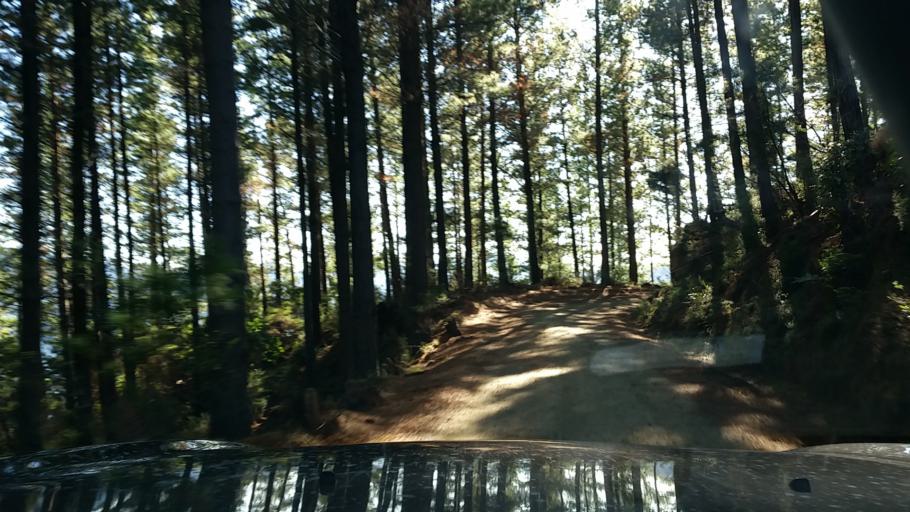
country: NZ
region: Marlborough
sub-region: Marlborough District
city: Picton
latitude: -41.1209
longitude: 173.9888
